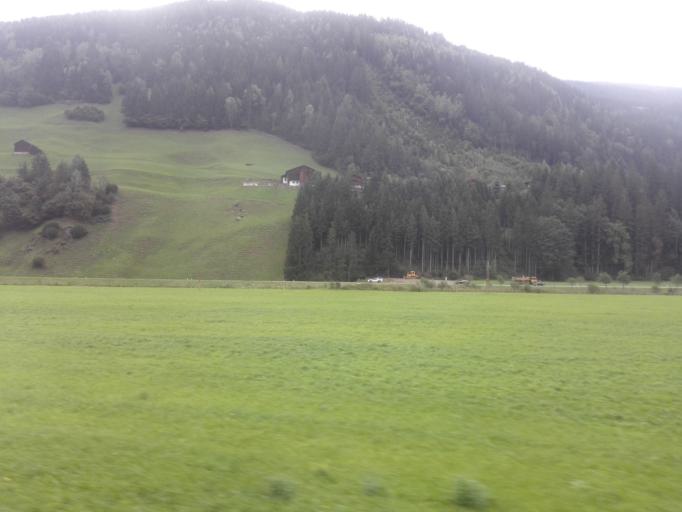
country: AT
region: Salzburg
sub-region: Politischer Bezirk Zell am See
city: Bramberg am Wildkogel
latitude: 47.2571
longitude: 12.3169
